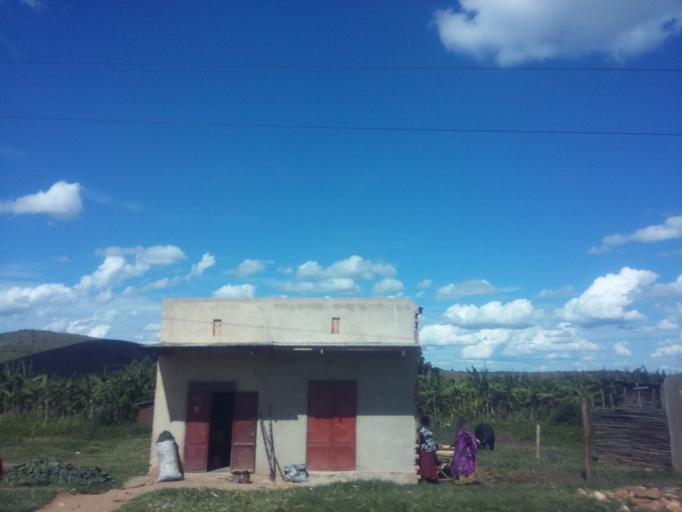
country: UG
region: Western Region
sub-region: Ntungamo District
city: Ntungamo
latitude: -0.9657
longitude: 30.2045
